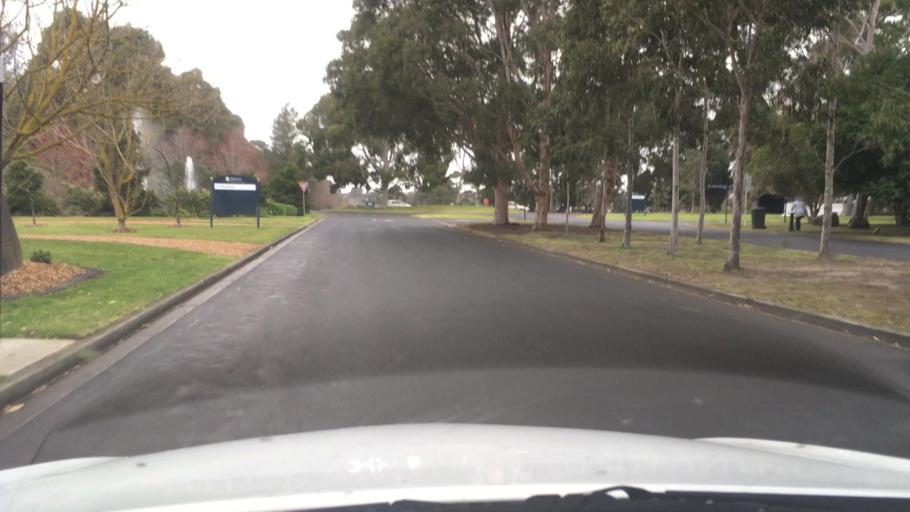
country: AU
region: Victoria
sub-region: Greater Dandenong
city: Noble Park North
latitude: -37.9401
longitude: 145.1777
